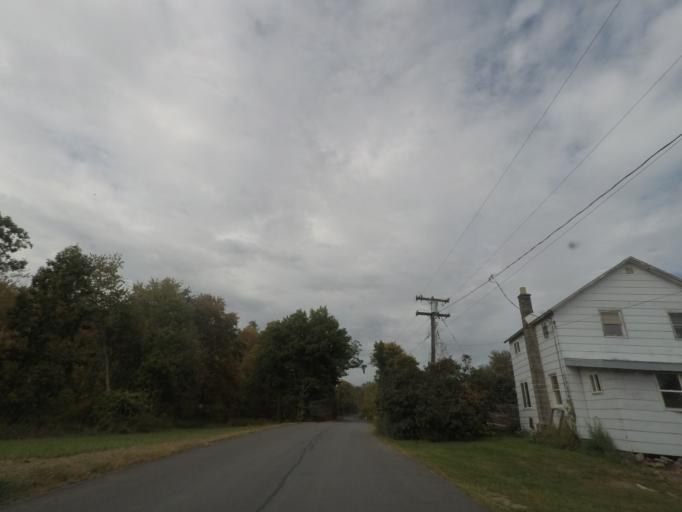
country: US
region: New York
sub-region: Rensselaer County
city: Nassau
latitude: 42.5342
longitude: -73.6447
